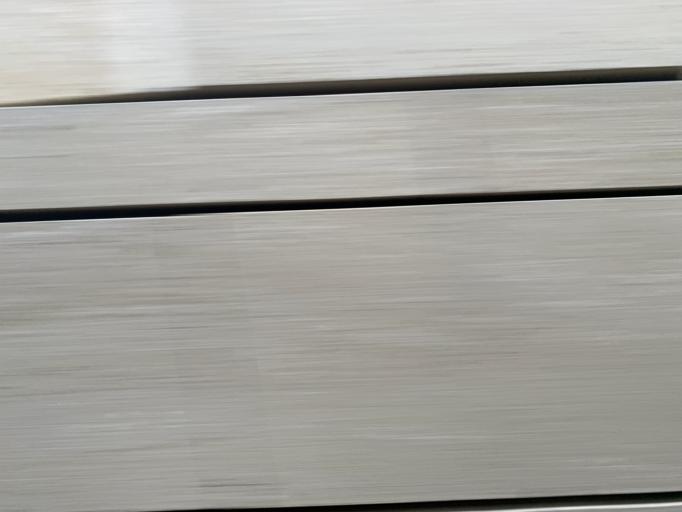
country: FR
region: Rhone-Alpes
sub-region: Departement du Rhone
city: Meyzieu
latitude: 45.7706
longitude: 5.0071
